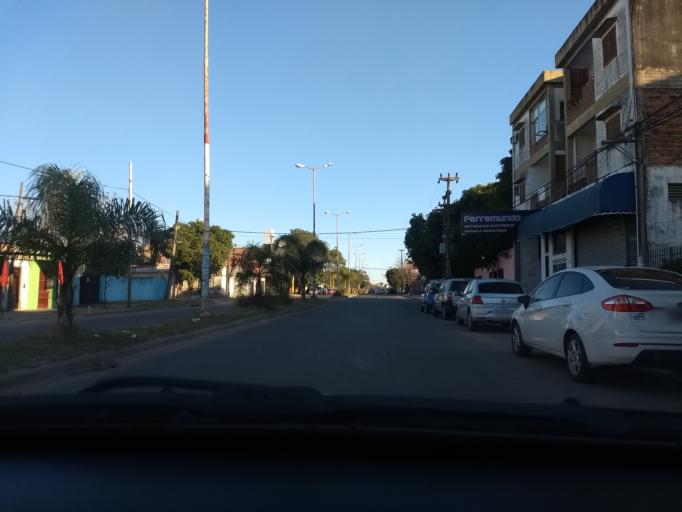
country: AR
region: Corrientes
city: Corrientes
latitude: -27.4739
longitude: -58.8135
